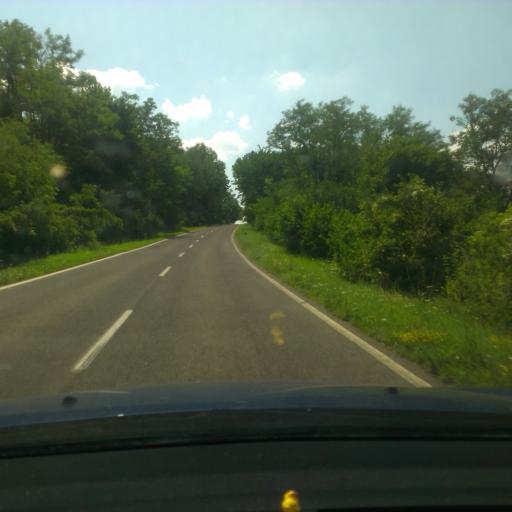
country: SK
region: Trnavsky
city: Hlohovec
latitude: 48.4905
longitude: 17.8130
